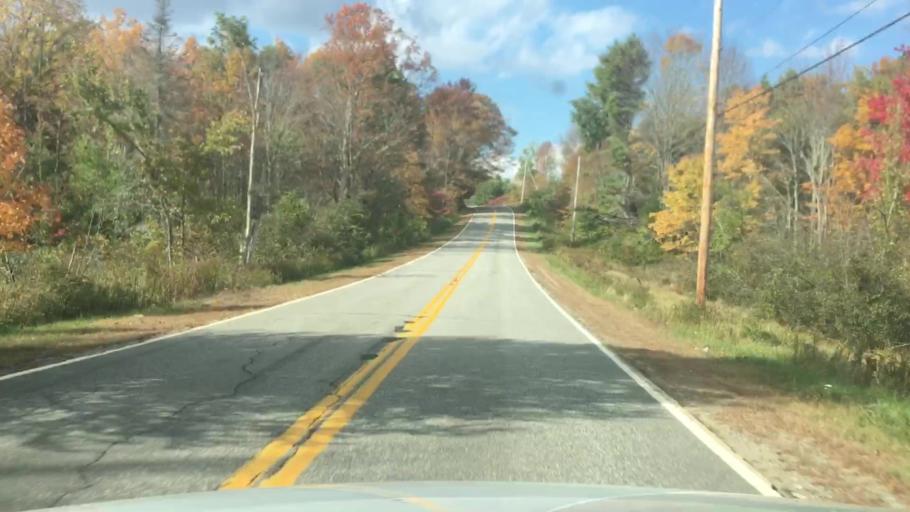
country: US
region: Maine
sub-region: Knox County
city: Washington
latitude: 44.3169
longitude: -69.3555
